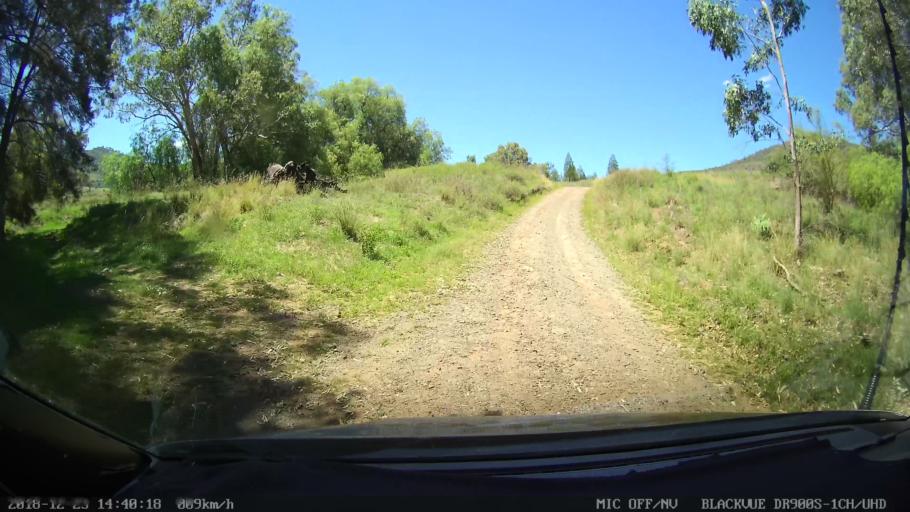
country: AU
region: New South Wales
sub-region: Tamworth Municipality
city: Manilla
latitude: -30.6275
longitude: 150.9018
